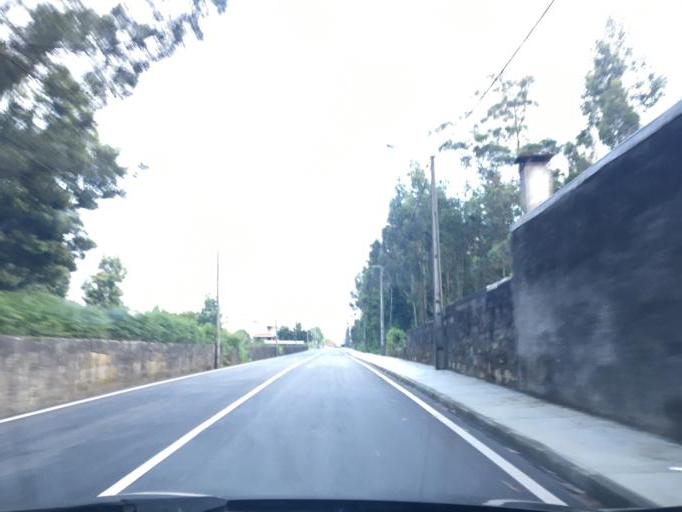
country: PT
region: Porto
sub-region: Maia
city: Anta
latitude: 41.2510
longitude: -8.6379
